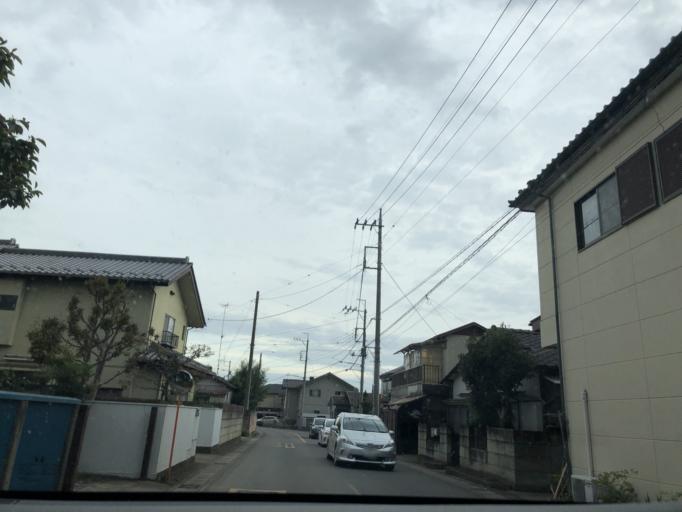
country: JP
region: Tochigi
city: Sano
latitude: 36.3070
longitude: 139.5711
